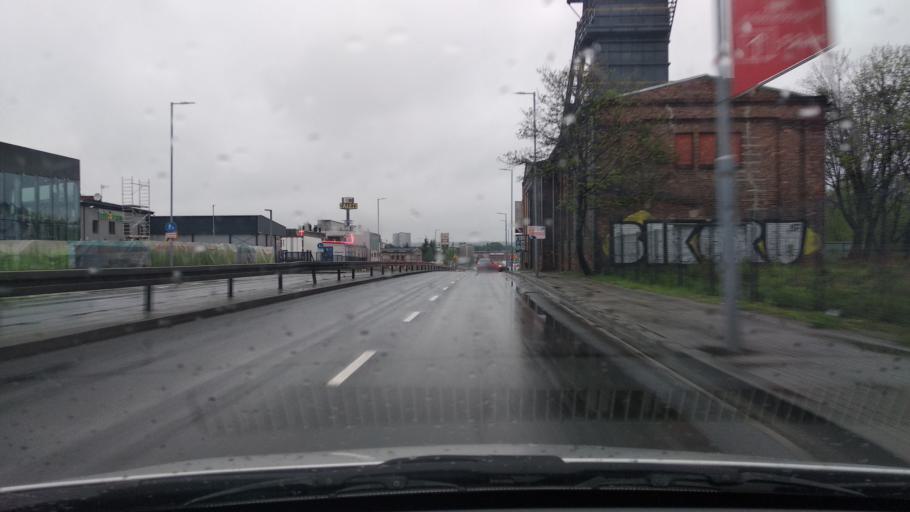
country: PL
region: Silesian Voivodeship
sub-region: Katowice
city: Katowice
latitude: 50.2593
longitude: 18.9855
